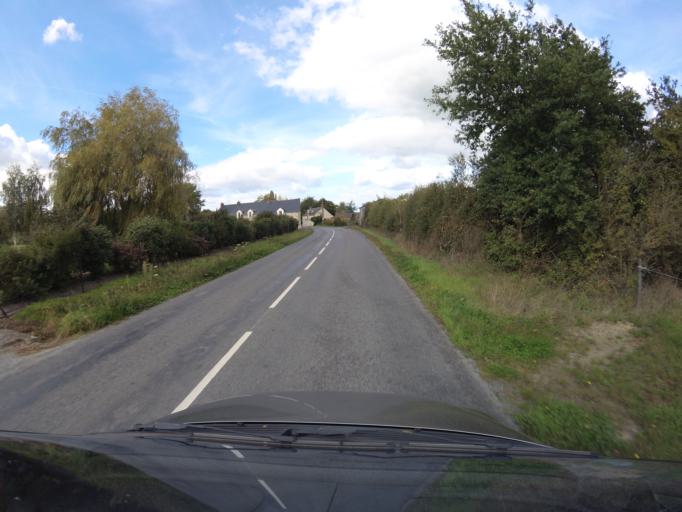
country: FR
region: Pays de la Loire
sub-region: Departement de la Loire-Atlantique
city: Casson
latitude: 47.3748
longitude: -1.5534
